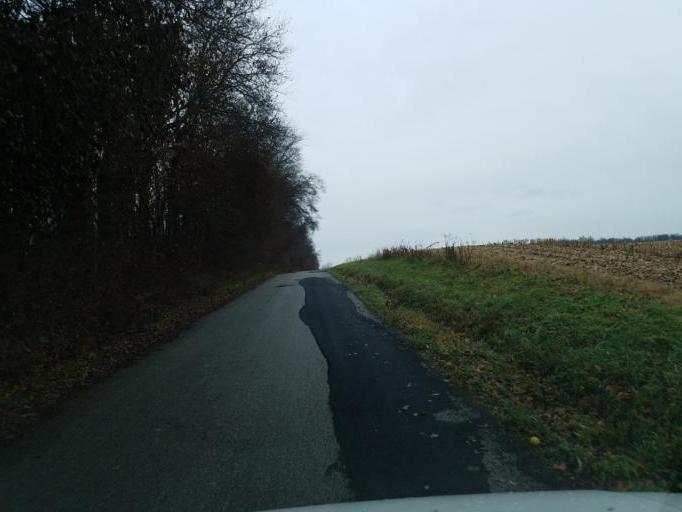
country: US
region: Ohio
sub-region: Knox County
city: Fredericktown
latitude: 40.5079
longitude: -82.5711
